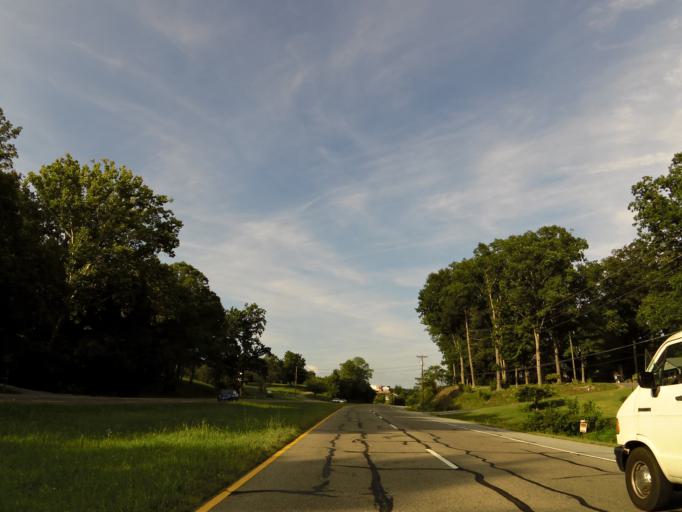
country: US
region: Tennessee
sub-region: Sevier County
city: Sevierville
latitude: 35.8678
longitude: -83.6019
